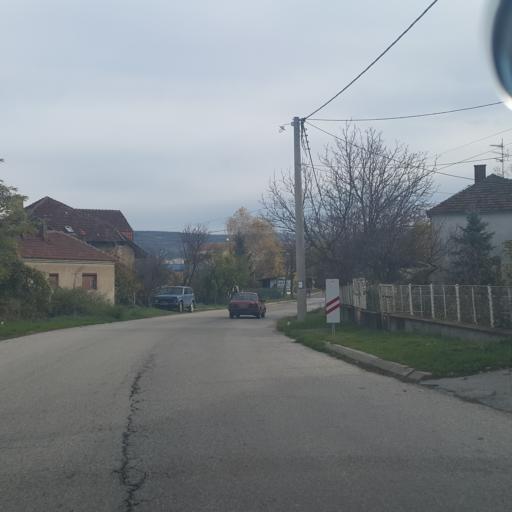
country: RS
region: Central Serbia
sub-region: Zajecarski Okrug
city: Knjazevac
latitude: 43.5705
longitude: 22.2478
